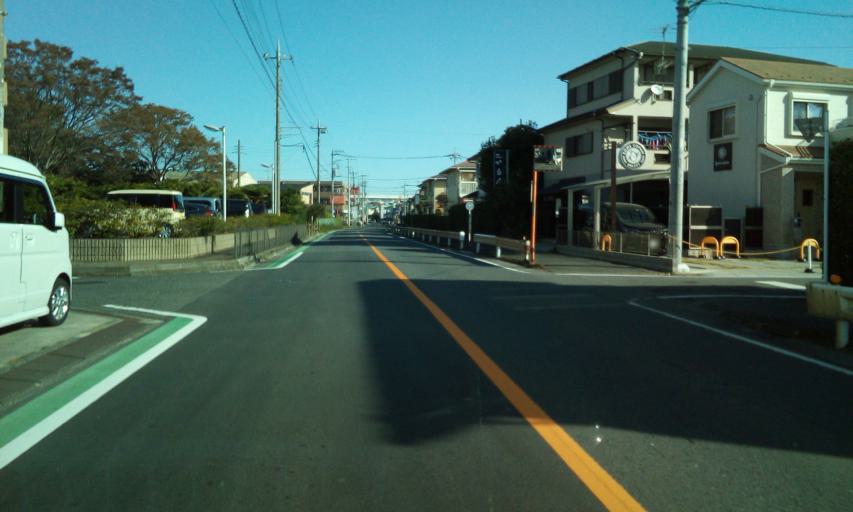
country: JP
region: Chiba
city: Nagareyama
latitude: 35.8586
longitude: 139.8860
